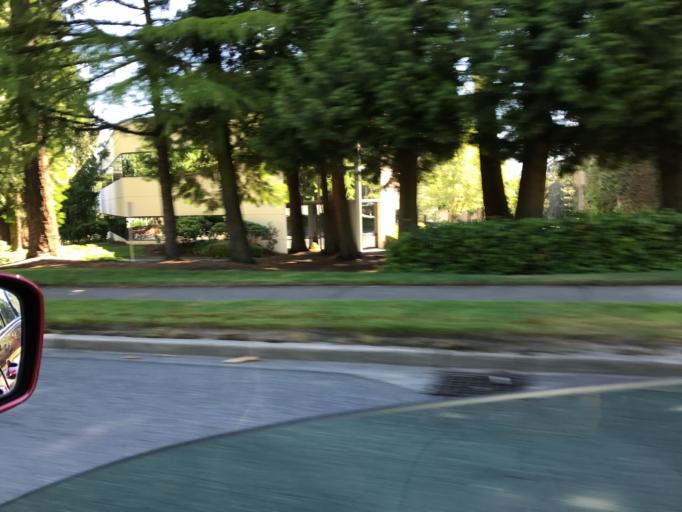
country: US
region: Washington
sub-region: King County
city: Redmond
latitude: 47.6515
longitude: -122.1432
